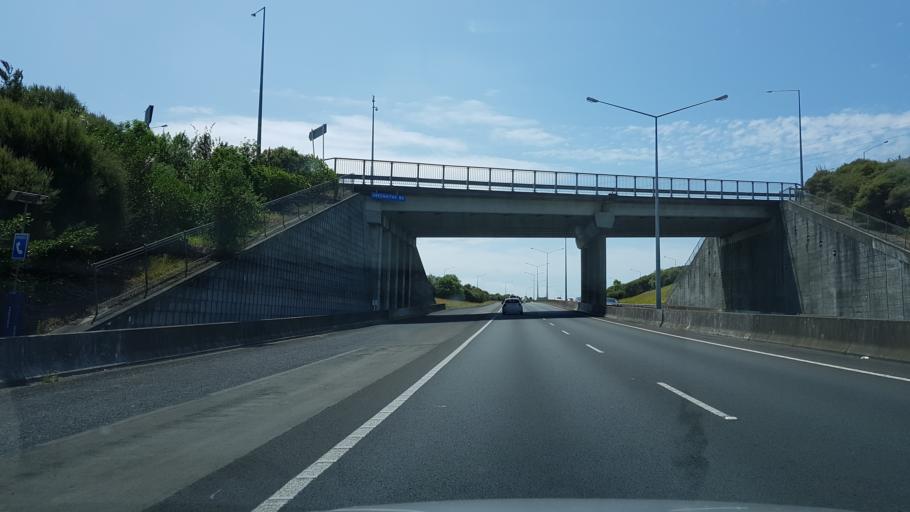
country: NZ
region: Auckland
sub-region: Auckland
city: North Shore
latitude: -36.7726
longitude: 174.6853
